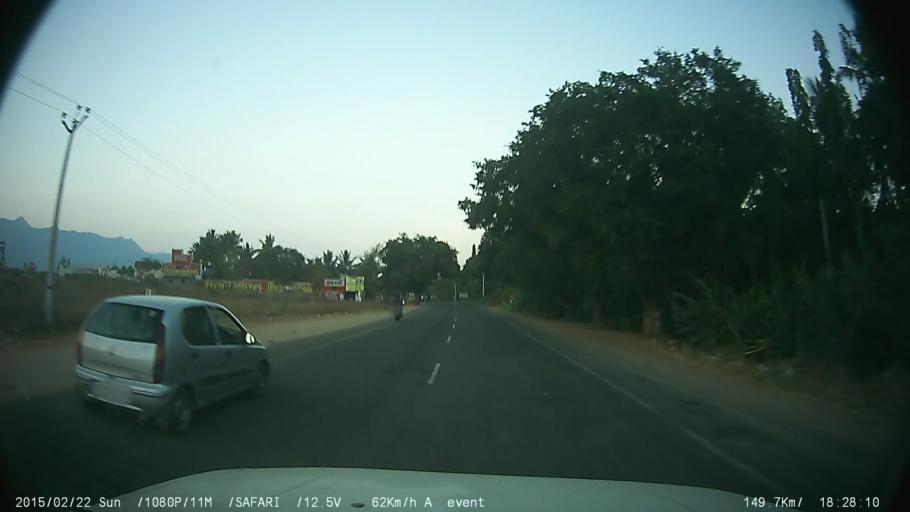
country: IN
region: Tamil Nadu
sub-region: Theni
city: Teni
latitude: 9.9753
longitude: 77.4471
